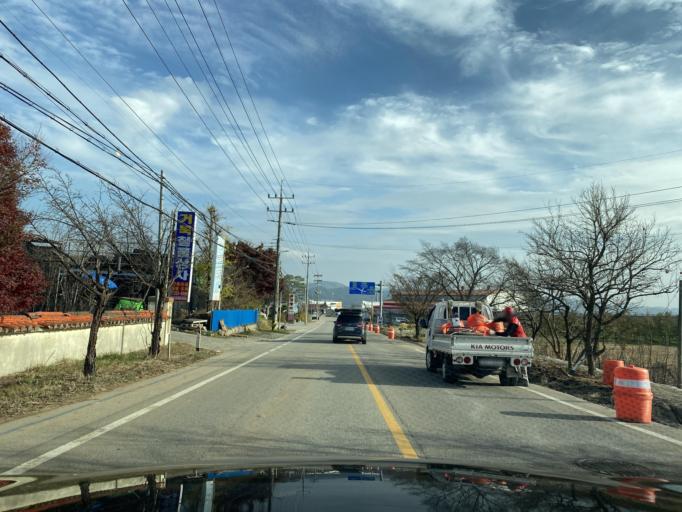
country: KR
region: Chungcheongnam-do
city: Yesan
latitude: 36.6860
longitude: 126.8019
